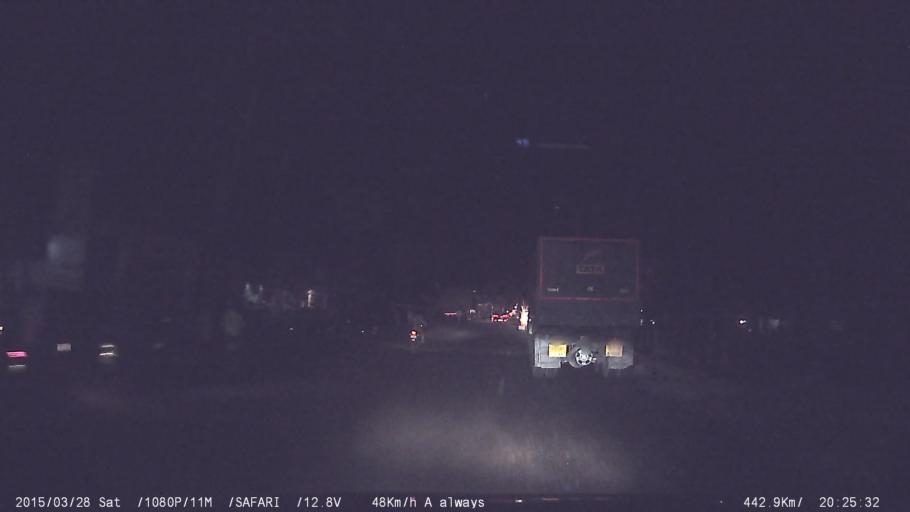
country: IN
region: Karnataka
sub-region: Mandya
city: Maddur
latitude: 12.5995
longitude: 77.0528
